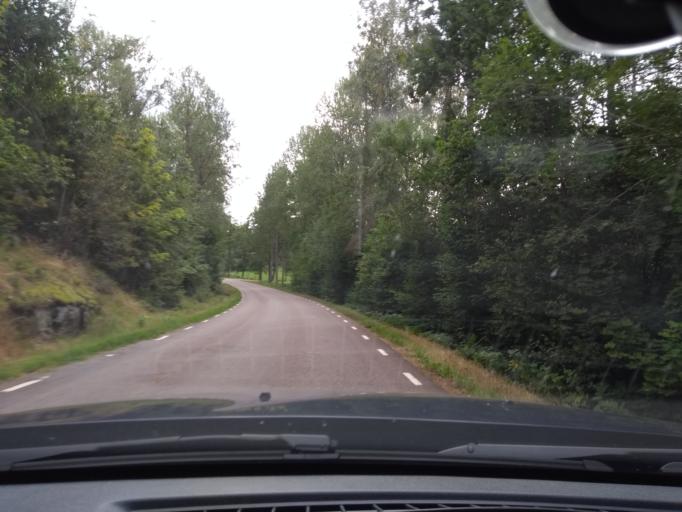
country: SE
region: Joenkoeping
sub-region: Eksjo Kommun
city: Mariannelund
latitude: 57.6259
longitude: 15.7082
